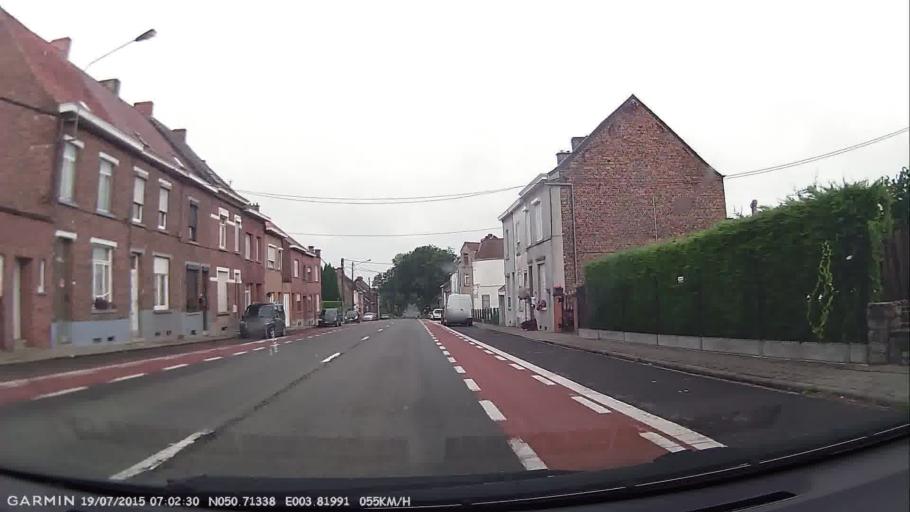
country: BE
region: Wallonia
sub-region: Province du Hainaut
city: Lessines
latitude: 50.7134
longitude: 3.8197
